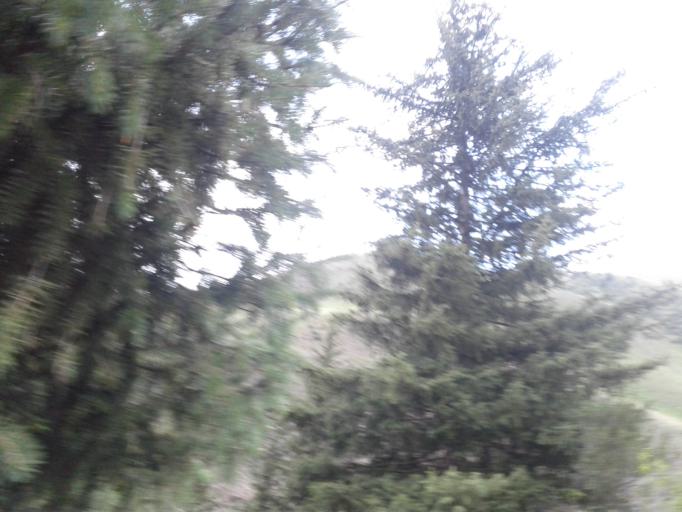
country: KG
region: Naryn
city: Naryn
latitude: 41.4541
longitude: 76.4532
